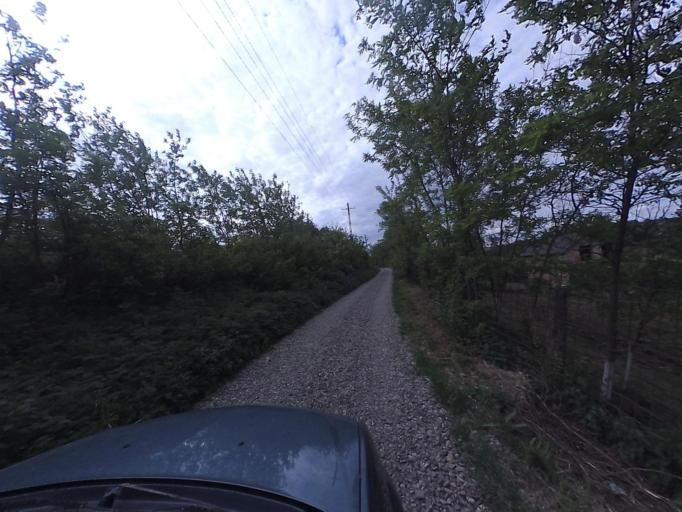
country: RO
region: Neamt
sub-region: Comuna Dulcesti
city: Dulcesti
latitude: 46.9583
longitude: 26.7871
